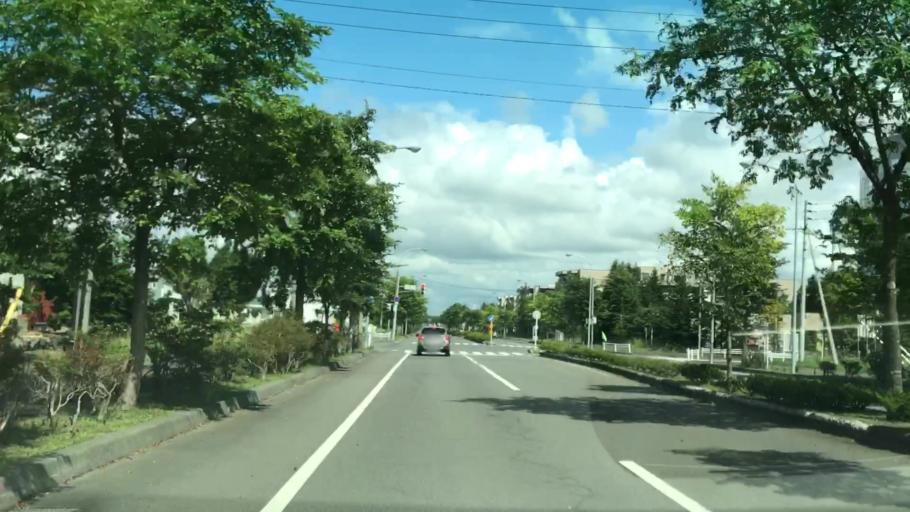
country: JP
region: Hokkaido
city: Chitose
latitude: 42.7785
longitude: 141.5998
